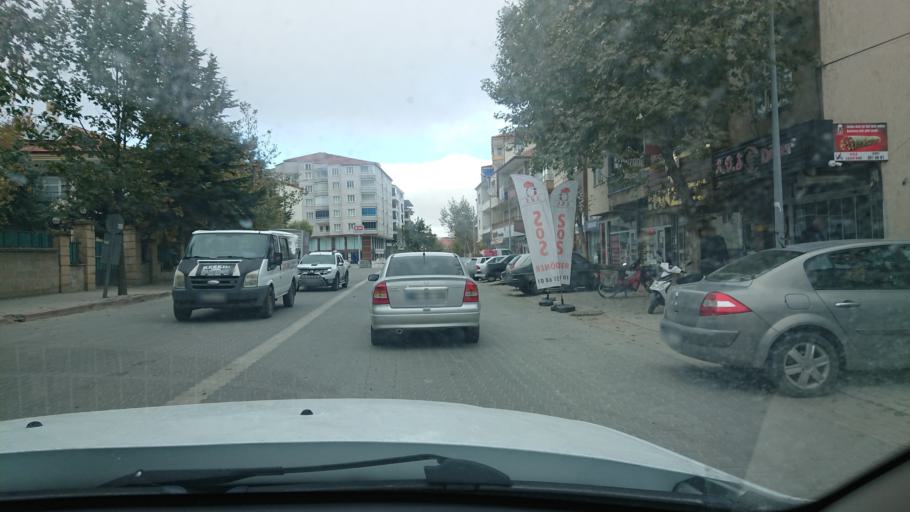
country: TR
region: Aksaray
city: Ortakoy
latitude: 38.7381
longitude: 34.0386
